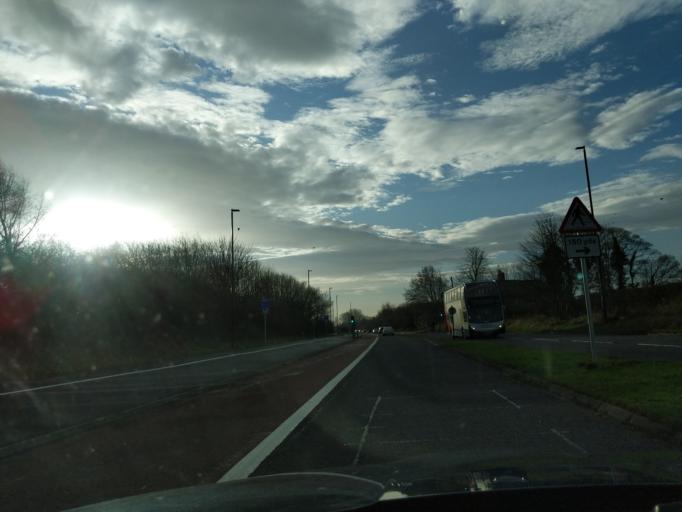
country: GB
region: England
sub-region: Newcastle upon Tyne
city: Gosforth
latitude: 55.0171
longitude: -1.5989
